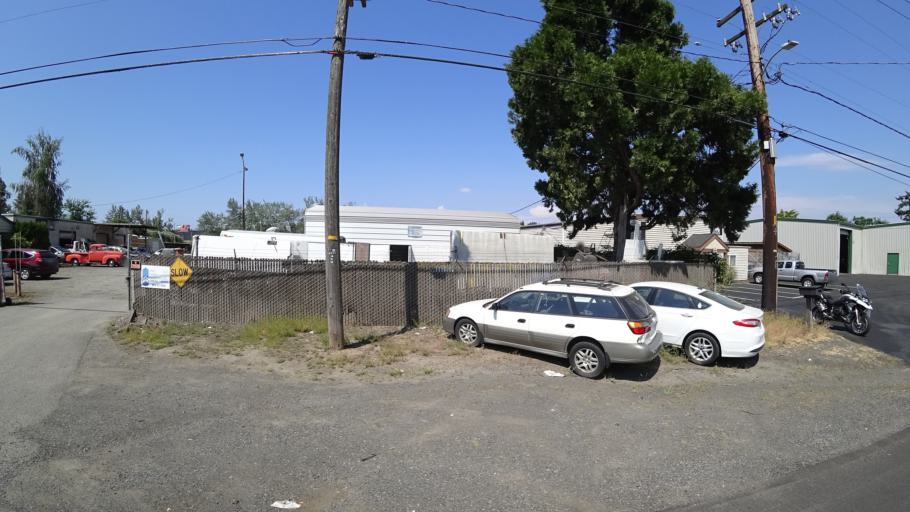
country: US
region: Oregon
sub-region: Multnomah County
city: Lents
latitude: 45.5618
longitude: -122.5560
